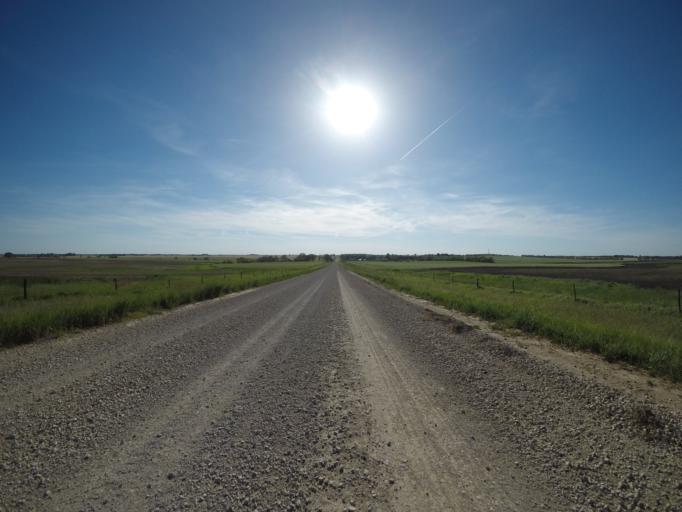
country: US
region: Kansas
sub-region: Clay County
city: Clay Center
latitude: 39.5098
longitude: -97.0759
